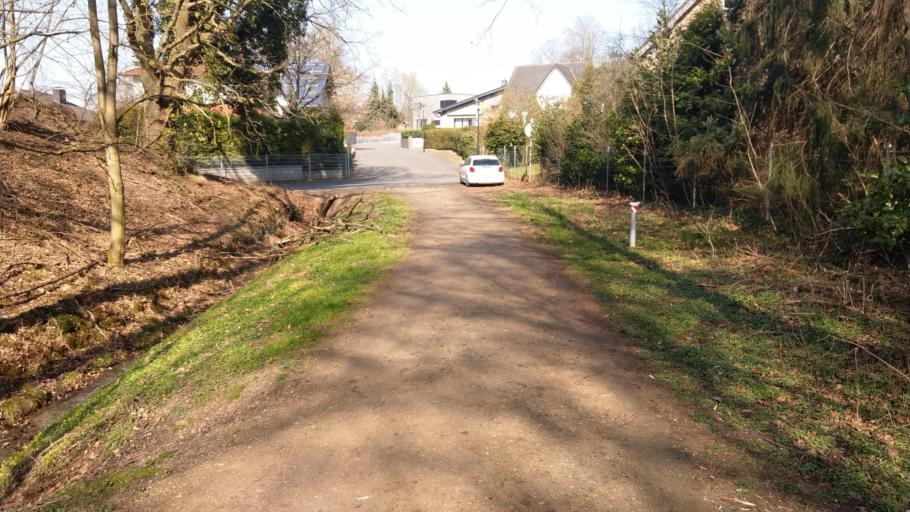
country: DE
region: North Rhine-Westphalia
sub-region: Regierungsbezirk Koln
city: Wassenberg
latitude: 51.1096
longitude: 6.1588
